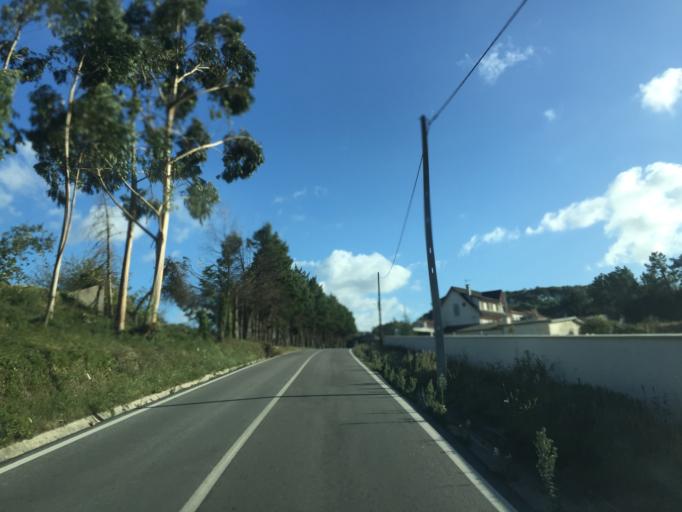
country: PT
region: Coimbra
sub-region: Figueira da Foz
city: Tavarede
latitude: 40.1992
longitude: -8.8354
